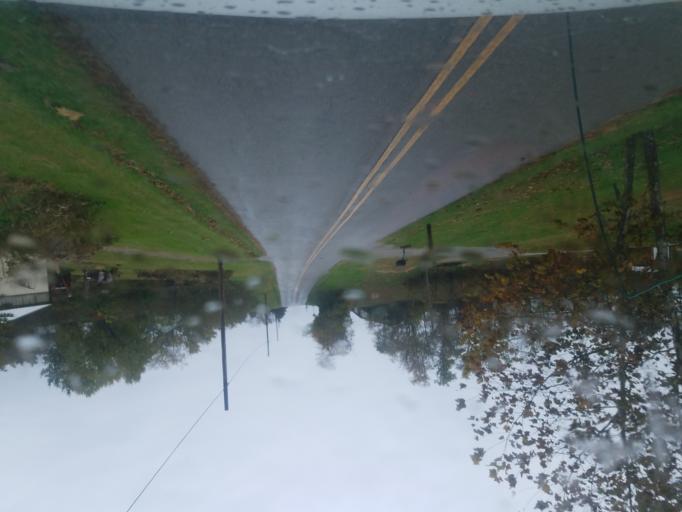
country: US
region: Ohio
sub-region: Washington County
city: Beverly
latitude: 39.4474
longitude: -81.6233
